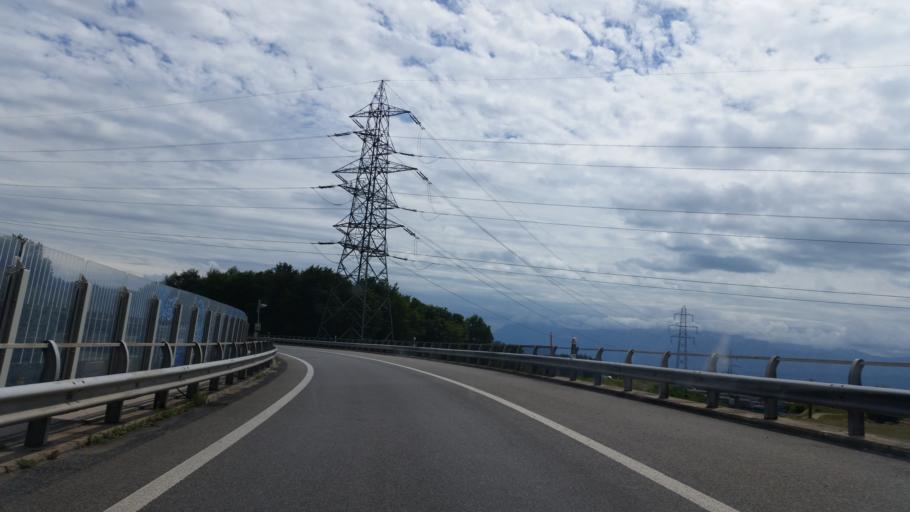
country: CH
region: Vaud
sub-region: Ouest Lausannois District
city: Bussigny
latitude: 46.5630
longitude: 6.5588
